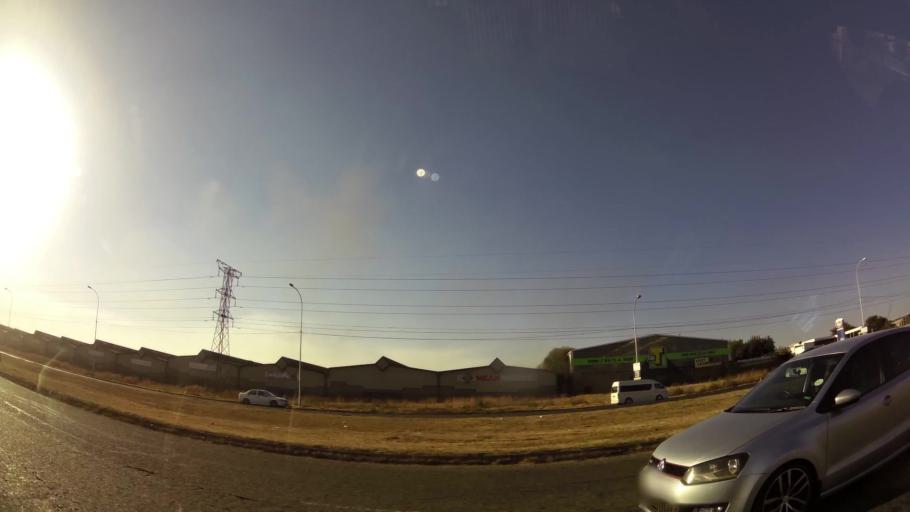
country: ZA
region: Gauteng
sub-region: City of Johannesburg Metropolitan Municipality
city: Roodepoort
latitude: -26.1902
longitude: 27.9153
